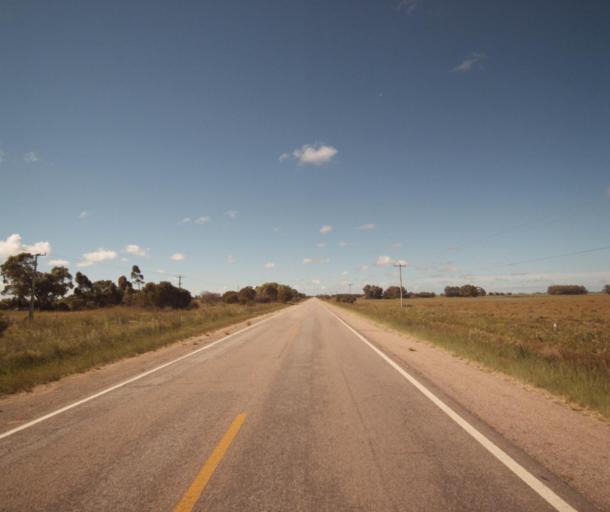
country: BR
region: Rio Grande do Sul
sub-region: Chui
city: Chui
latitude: -33.6401
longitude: -53.4214
